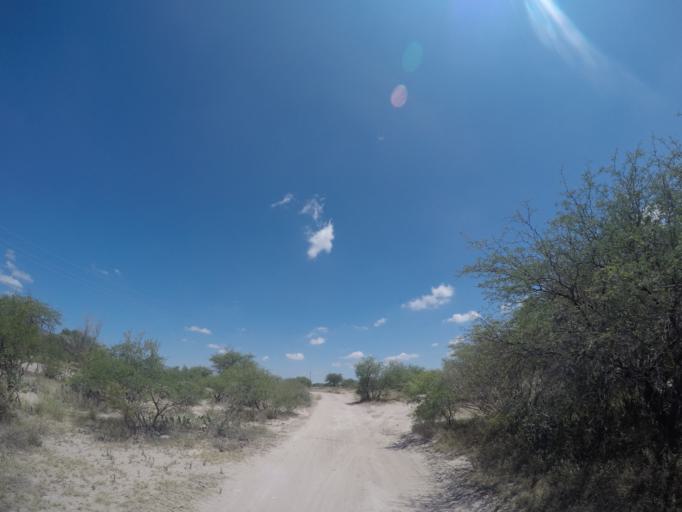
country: MX
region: San Luis Potosi
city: La Pila
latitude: 21.9863
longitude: -100.8964
